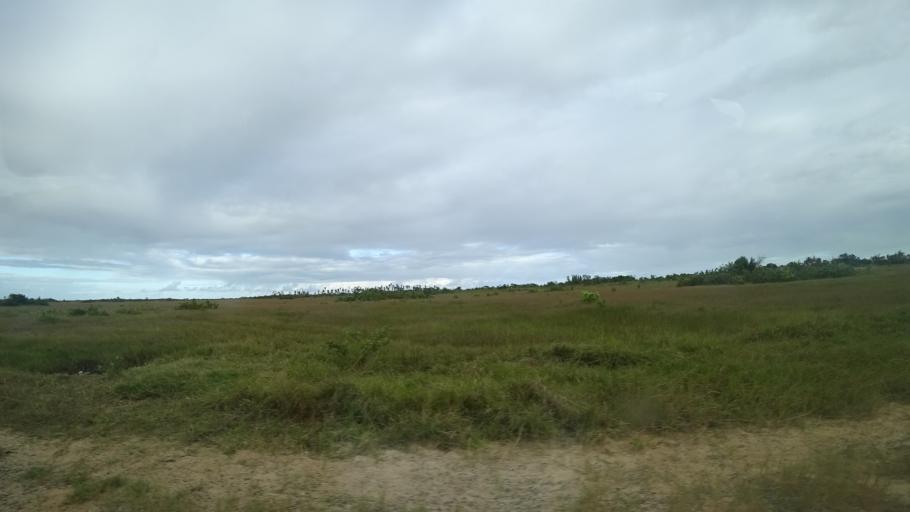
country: MZ
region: Sofala
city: Beira
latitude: -19.7109
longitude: 35.0167
